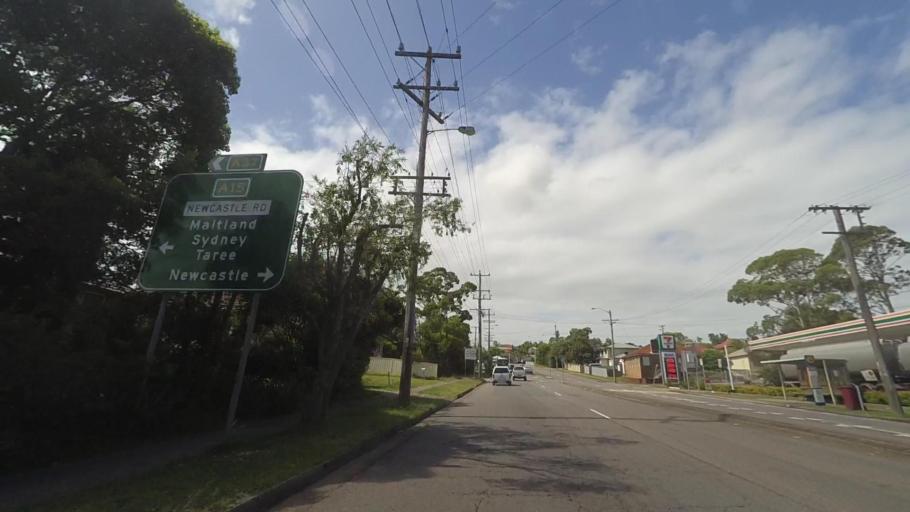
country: AU
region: New South Wales
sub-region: Newcastle
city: North Lambton
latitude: -32.9108
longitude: 151.7050
